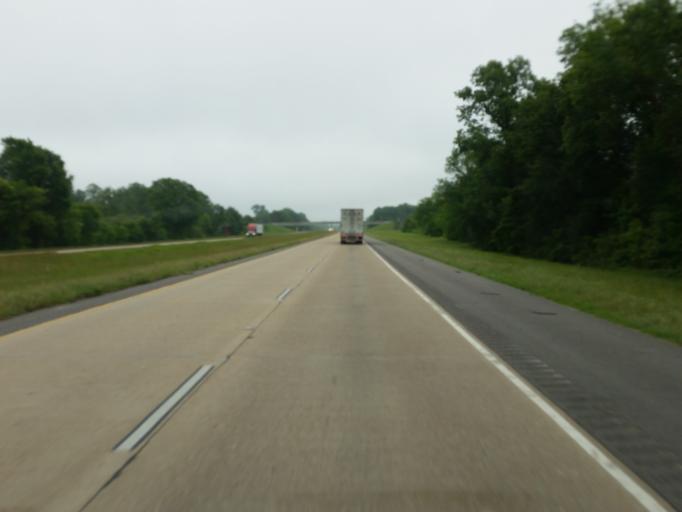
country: US
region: Louisiana
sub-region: Madison Parish
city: Tallulah
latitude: 32.3688
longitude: -91.1358
